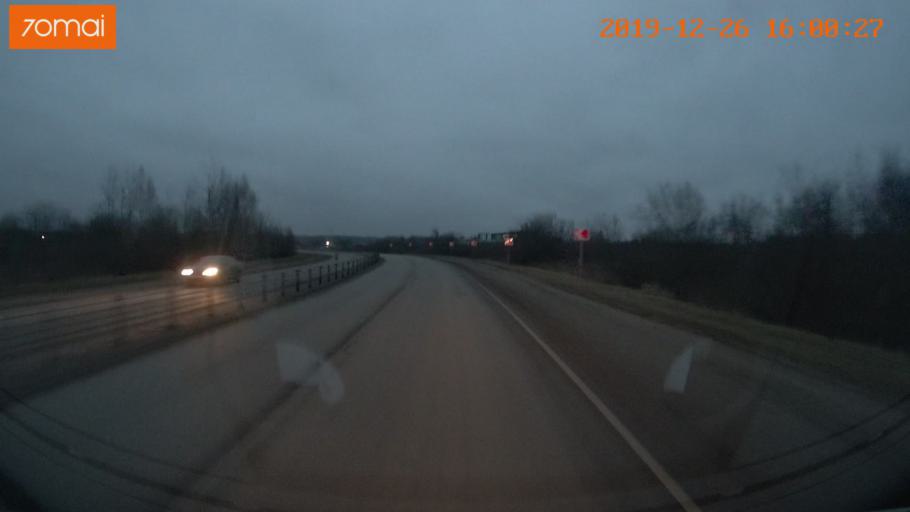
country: RU
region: Jaroslavl
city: Rybinsk
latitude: 58.0238
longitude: 38.8029
